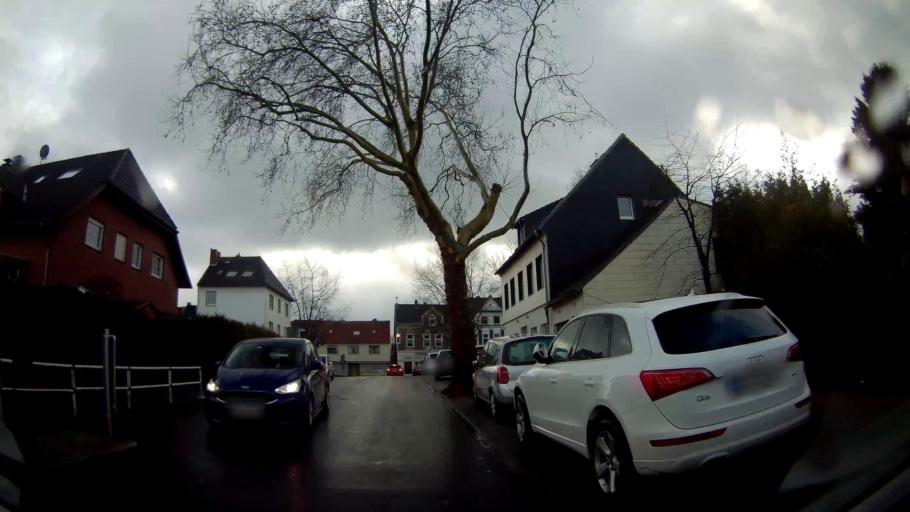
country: DE
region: North Rhine-Westphalia
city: Castrop-Rauxel
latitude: 51.5012
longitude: 7.2839
